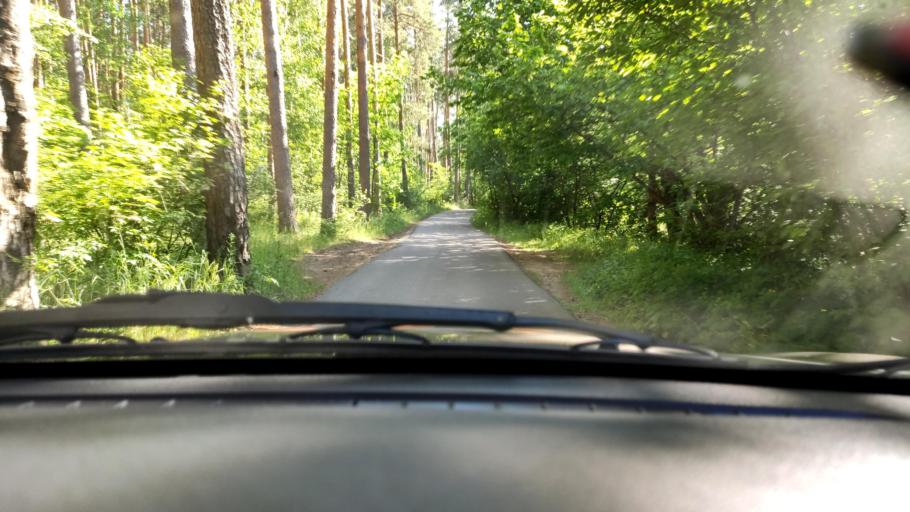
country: RU
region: Voronezj
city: Somovo
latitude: 51.8051
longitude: 39.3814
